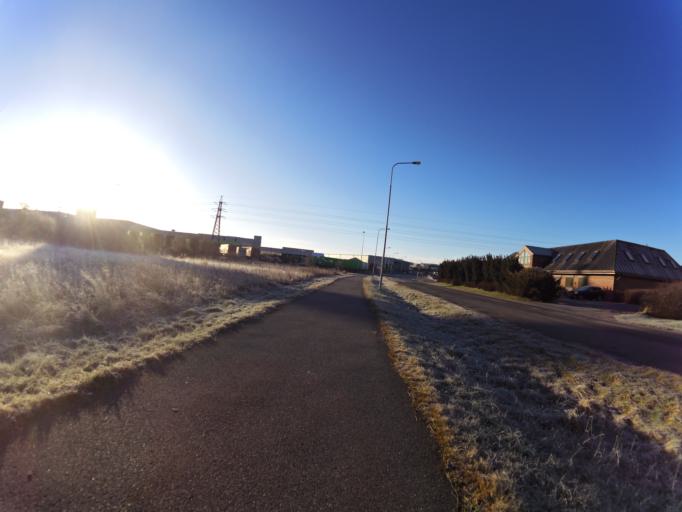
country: NO
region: Ostfold
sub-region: Fredrikstad
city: Fredrikstad
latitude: 59.2406
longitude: 10.9952
